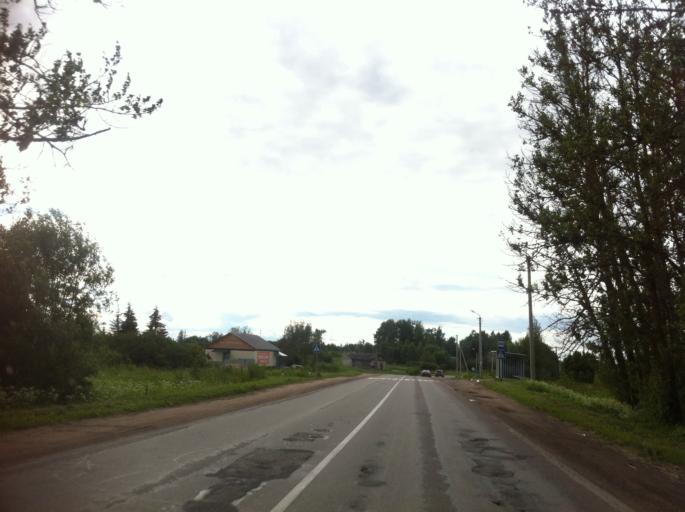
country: RU
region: Pskov
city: Pskov
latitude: 57.8106
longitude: 28.1635
